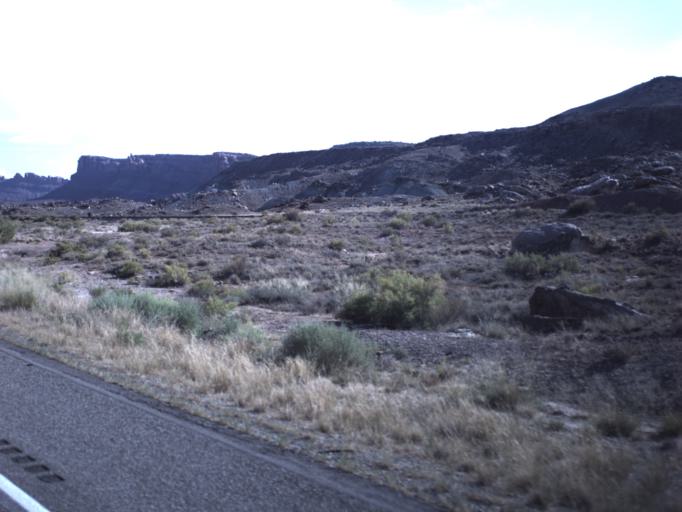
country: US
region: Utah
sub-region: Grand County
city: Moab
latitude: 38.7144
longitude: -109.7049
